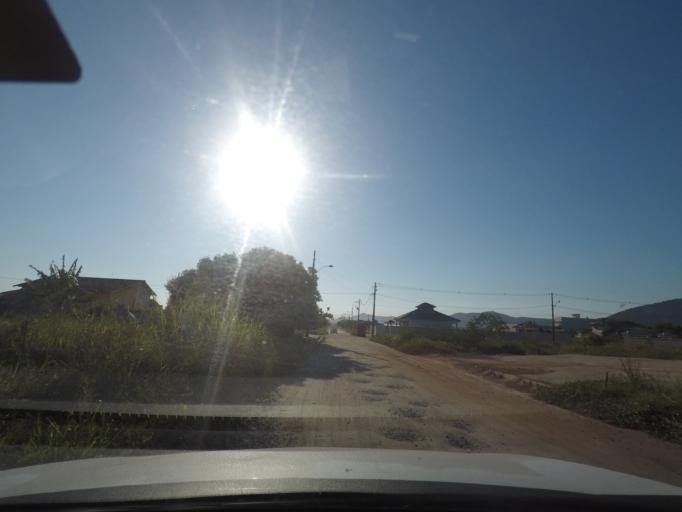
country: BR
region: Rio de Janeiro
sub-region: Marica
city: Marica
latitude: -22.9620
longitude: -42.9392
